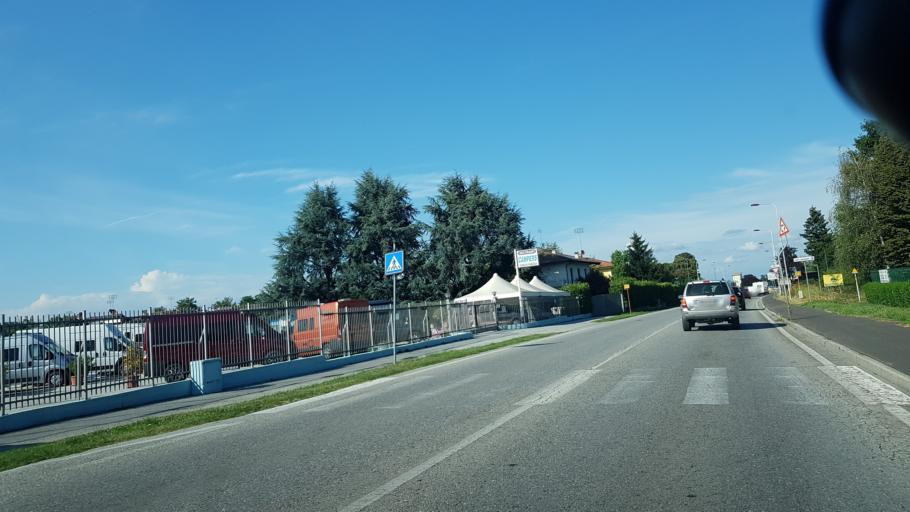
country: IT
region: Piedmont
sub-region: Provincia di Cuneo
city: Cuneo
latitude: 44.4056
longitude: 7.5473
